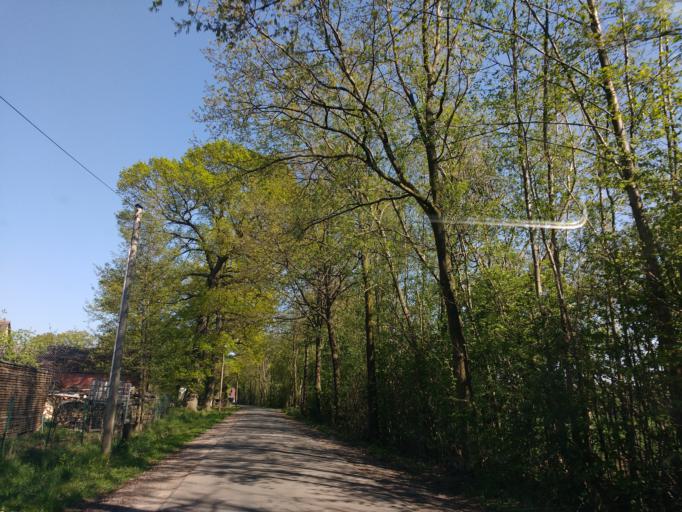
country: DE
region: North Rhine-Westphalia
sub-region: Regierungsbezirk Detmold
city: Delbruck
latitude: 51.7689
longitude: 8.5971
